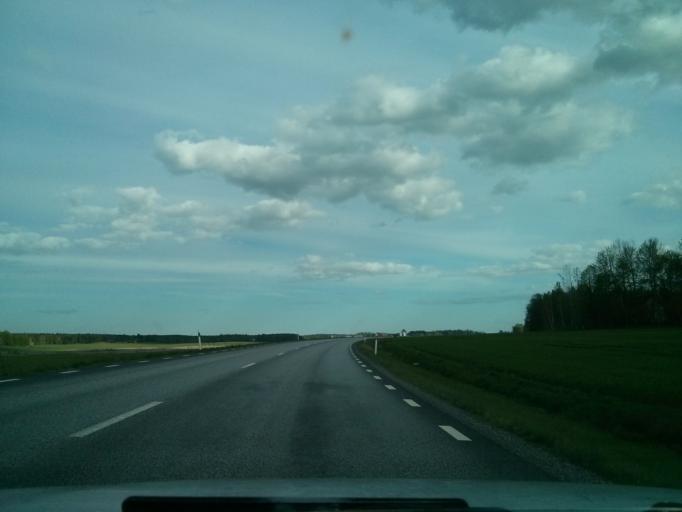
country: SE
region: Soedermanland
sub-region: Katrineholms Kommun
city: Katrineholm
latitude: 58.9665
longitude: 16.3642
